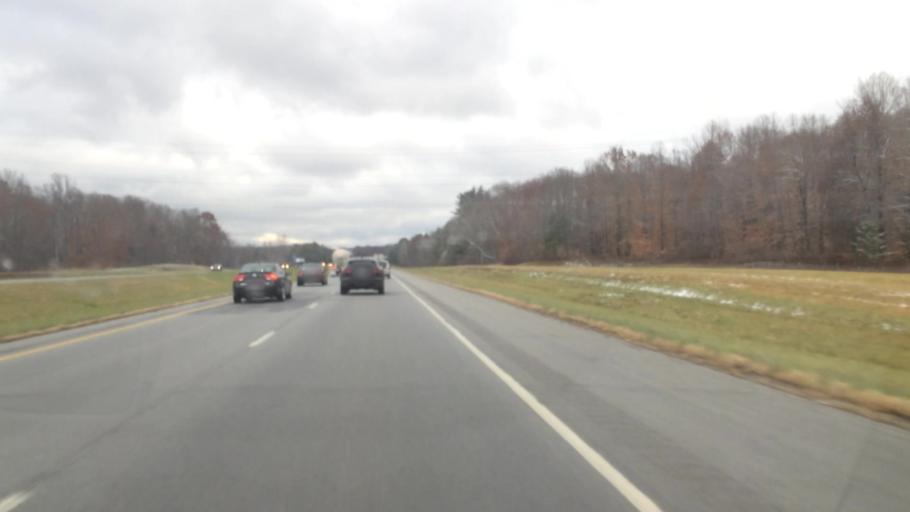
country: US
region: Ohio
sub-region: Summit County
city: Twinsburg
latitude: 41.2926
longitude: -81.4243
